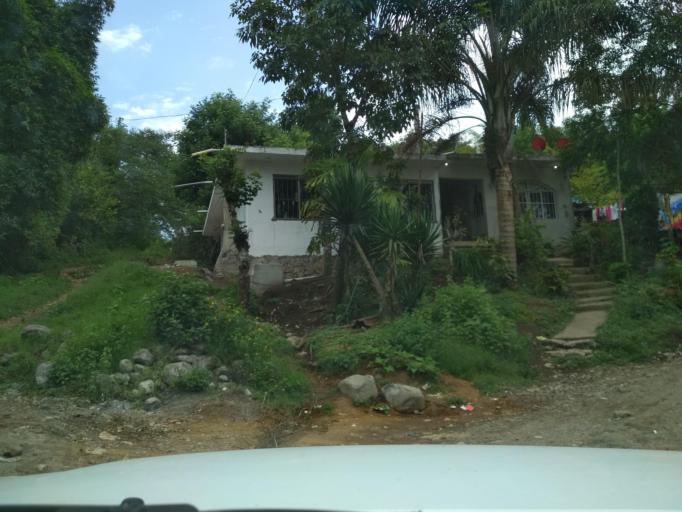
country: MX
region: Veracruz
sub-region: Mariano Escobedo
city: Mariano Escobedo
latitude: 18.9168
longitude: -97.1270
